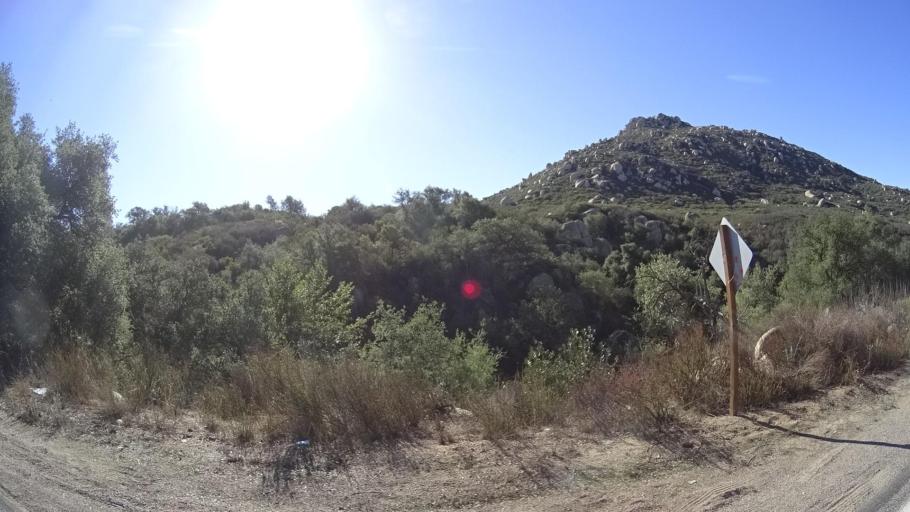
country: US
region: California
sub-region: San Diego County
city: Jamul
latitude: 32.6766
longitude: -116.7547
